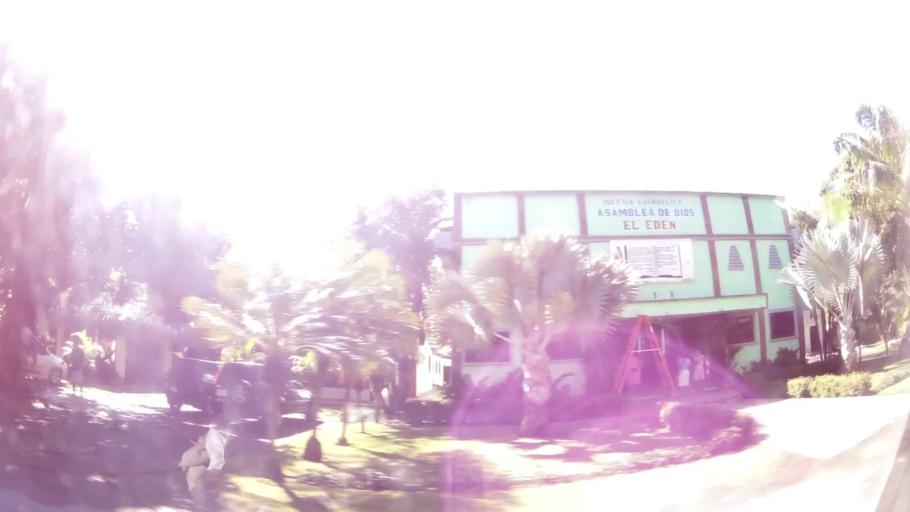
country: GT
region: Santa Rosa
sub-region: Municipio de Taxisco
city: Taxisco
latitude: 13.9073
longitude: -90.5152
